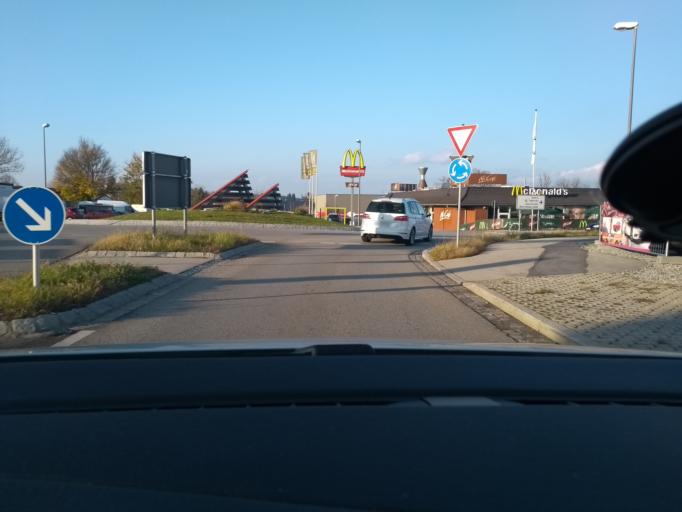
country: DE
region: Bavaria
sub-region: Upper Bavaria
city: Wasserburg am Inn
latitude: 48.0484
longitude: 12.2220
